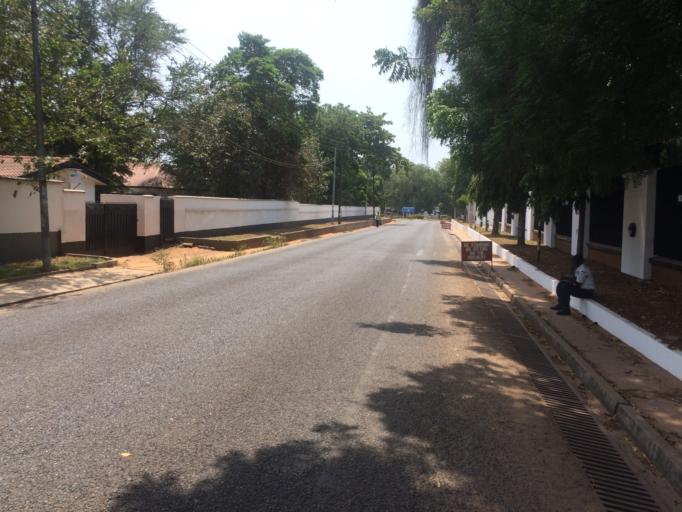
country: GH
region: Greater Accra
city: Accra
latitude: 5.5647
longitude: -0.1909
